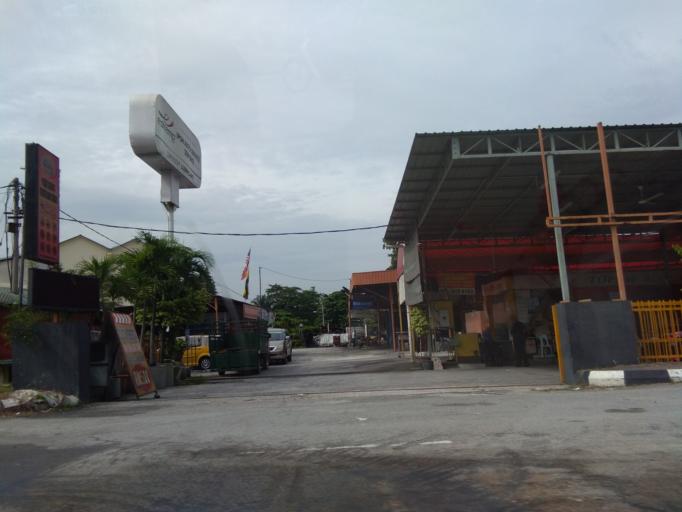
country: MY
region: Perak
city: Ipoh
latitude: 4.5960
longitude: 101.0871
